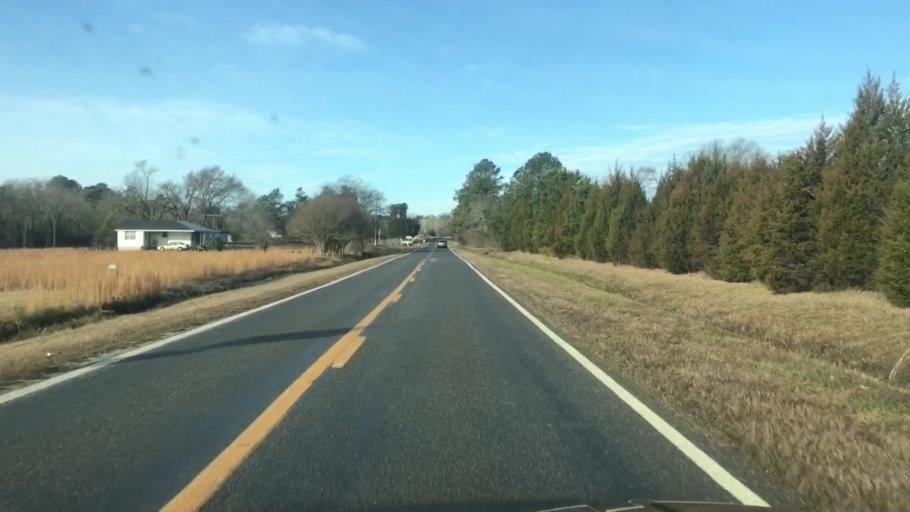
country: US
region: Arkansas
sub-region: Garland County
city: Rockwell
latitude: 34.4712
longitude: -93.2485
